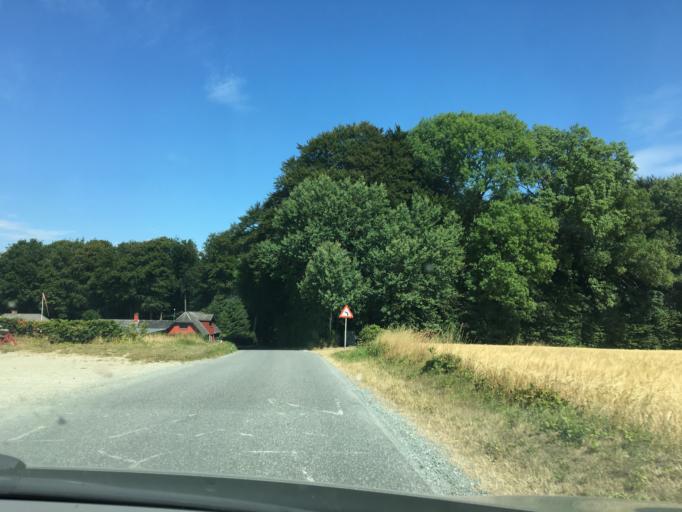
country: DK
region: South Denmark
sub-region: Middelfart Kommune
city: Norre Aby
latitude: 55.5037
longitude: 9.9032
